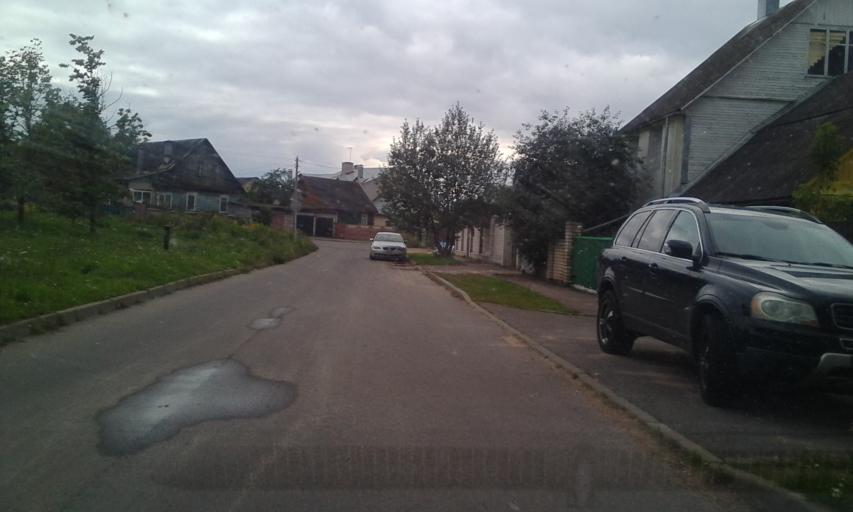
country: BY
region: Minsk
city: Minsk
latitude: 53.9453
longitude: 27.5752
